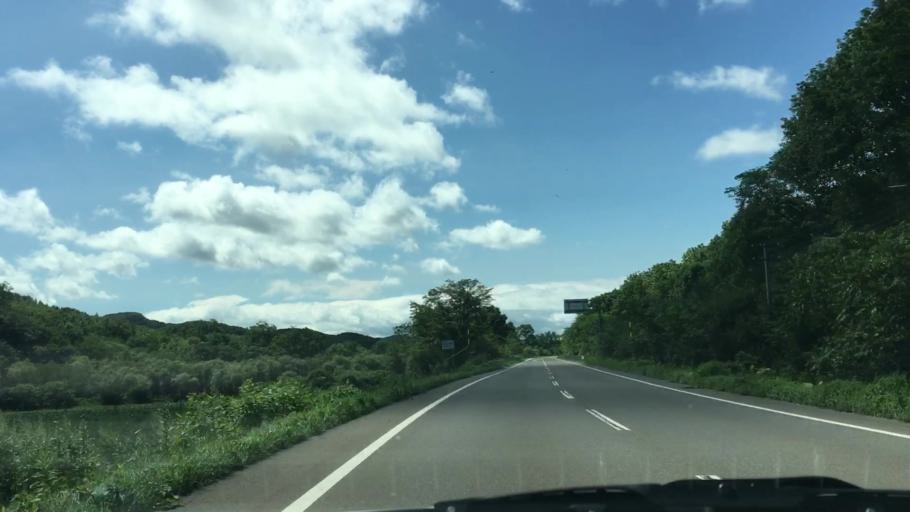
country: JP
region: Hokkaido
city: Otofuke
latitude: 43.2890
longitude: 143.6577
